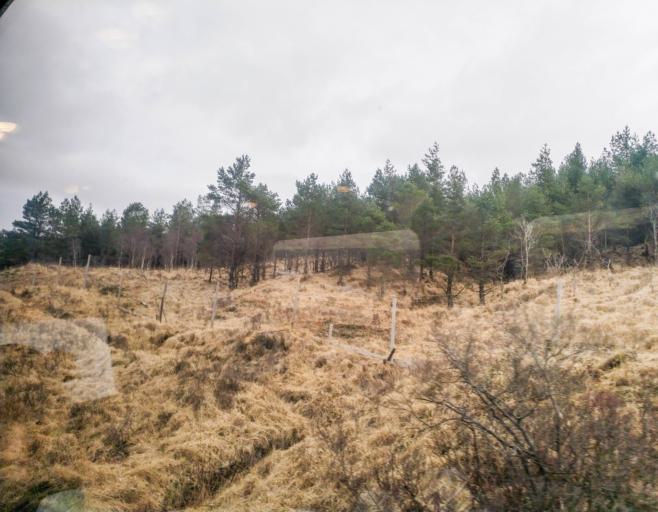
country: GB
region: Scotland
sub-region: Highland
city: Spean Bridge
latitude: 56.5283
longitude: -4.7626
